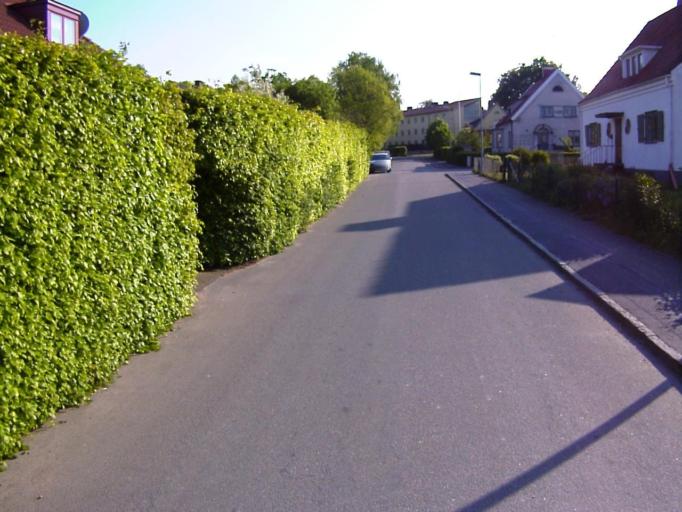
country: SE
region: Skane
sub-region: Kristianstads Kommun
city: Onnestad
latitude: 56.0603
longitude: 14.0277
